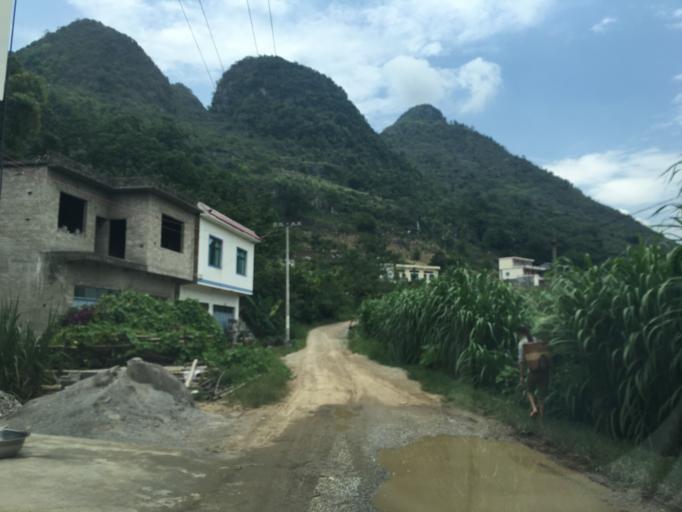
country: CN
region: Guangxi Zhuangzu Zizhiqu
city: Xinzhou
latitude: 25.2910
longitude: 105.6331
